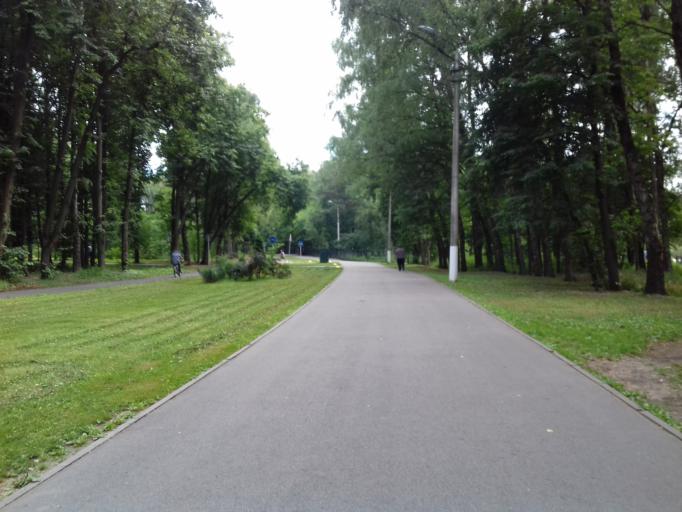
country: RU
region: Tula
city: Tula
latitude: 54.1795
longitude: 37.5826
